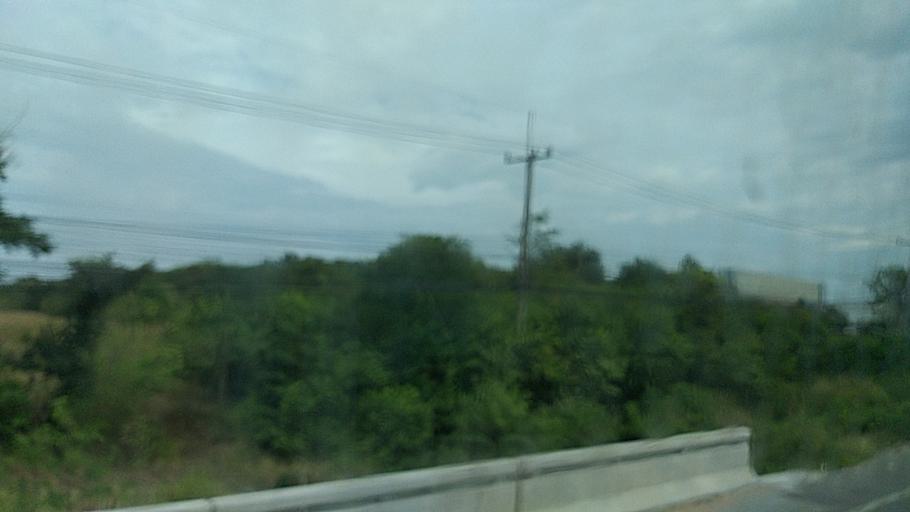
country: TH
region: Maha Sarakham
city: Maha Sarakham
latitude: 16.1631
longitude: 103.3434
